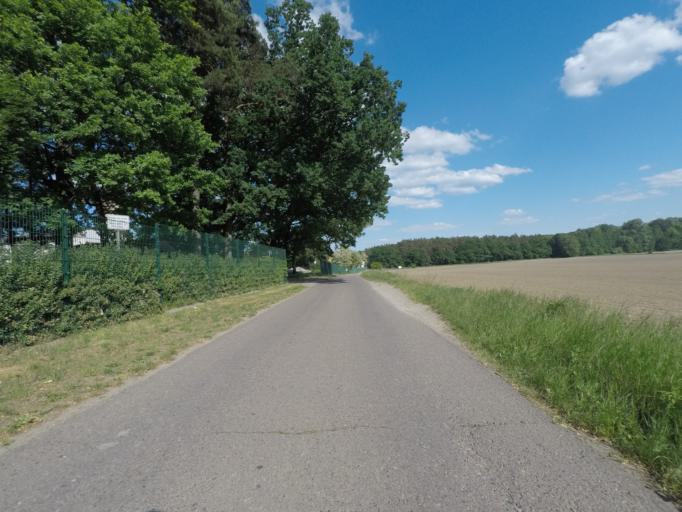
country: DE
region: Brandenburg
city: Britz
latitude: 52.8691
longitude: 13.7726
